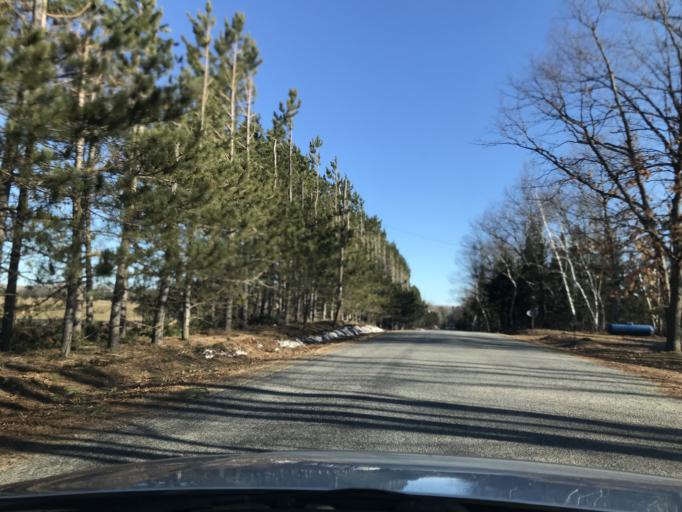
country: US
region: Wisconsin
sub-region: Marinette County
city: Niagara
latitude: 45.3598
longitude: -88.0296
